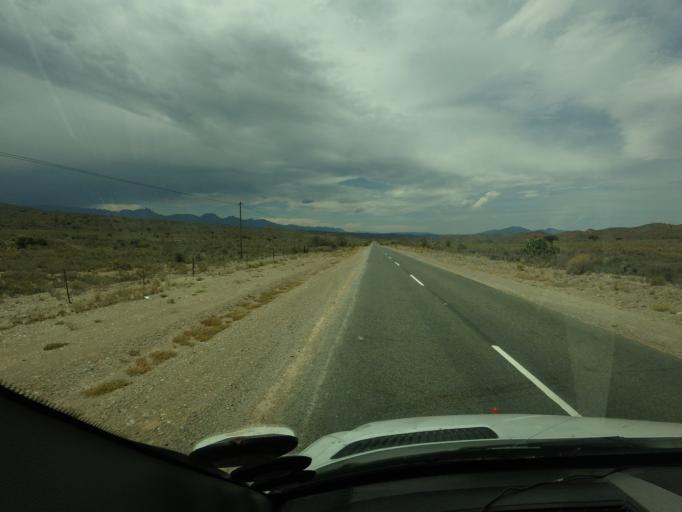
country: ZA
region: Western Cape
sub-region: Eden District Municipality
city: Ladismith
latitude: -33.6039
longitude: 21.0788
